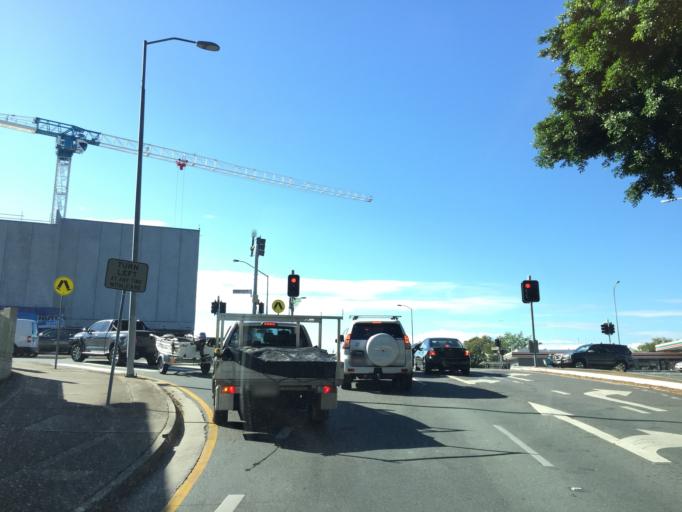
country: AU
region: Queensland
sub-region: Brisbane
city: Wilston
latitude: -27.4382
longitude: 153.0067
